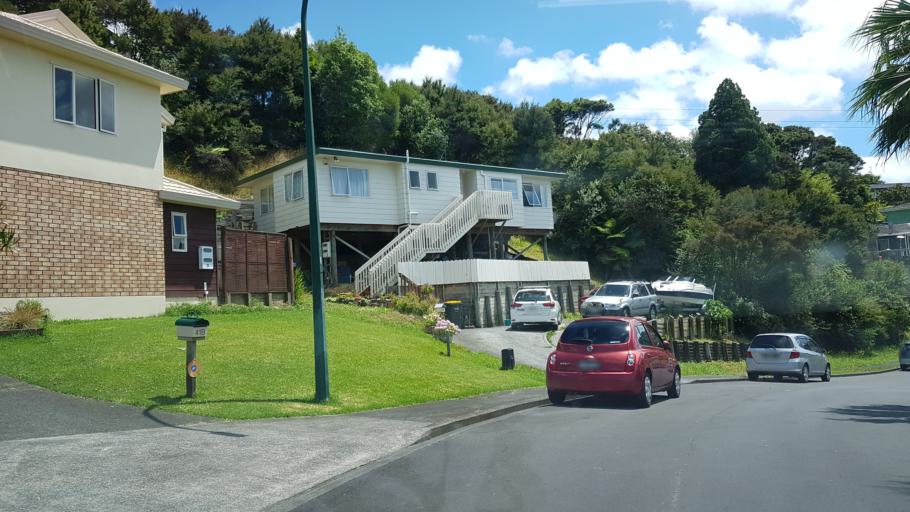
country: NZ
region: Auckland
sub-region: Auckland
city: North Shore
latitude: -36.7785
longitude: 174.7116
